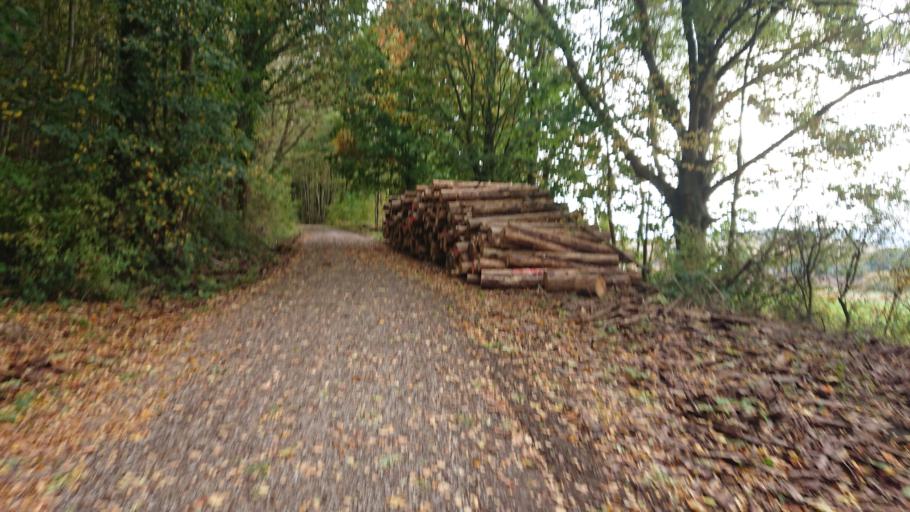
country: DE
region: Lower Saxony
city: Bovenden
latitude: 51.6053
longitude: 9.9514
